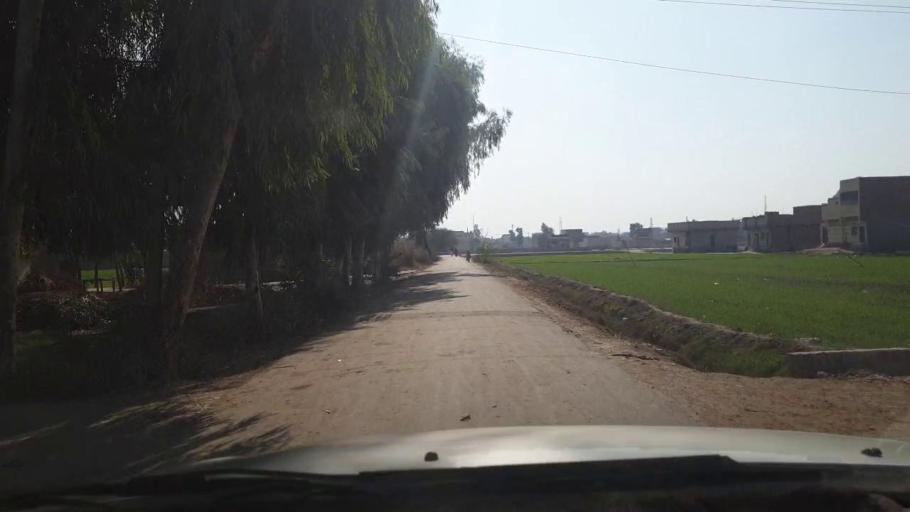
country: PK
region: Sindh
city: Mirpur Mathelo
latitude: 28.0324
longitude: 69.5516
